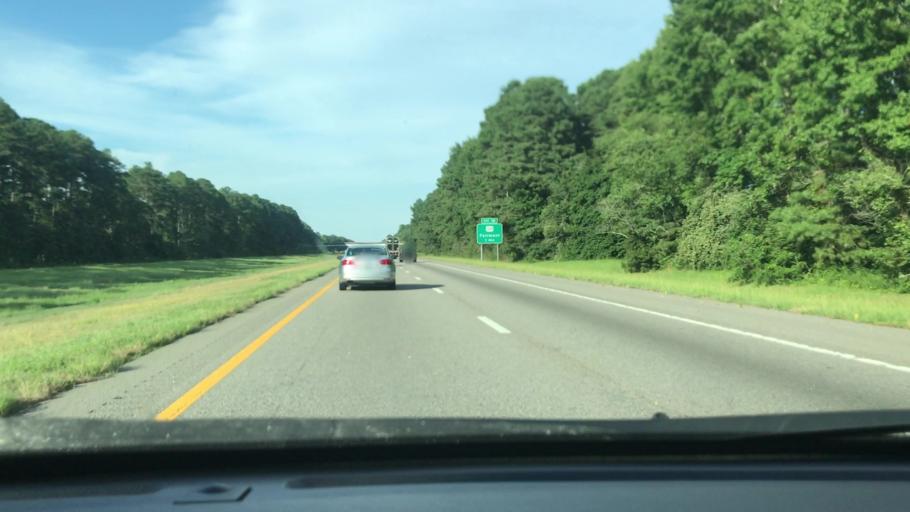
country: US
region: North Carolina
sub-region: Robeson County
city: Fairmont
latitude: 34.5661
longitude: -79.1702
